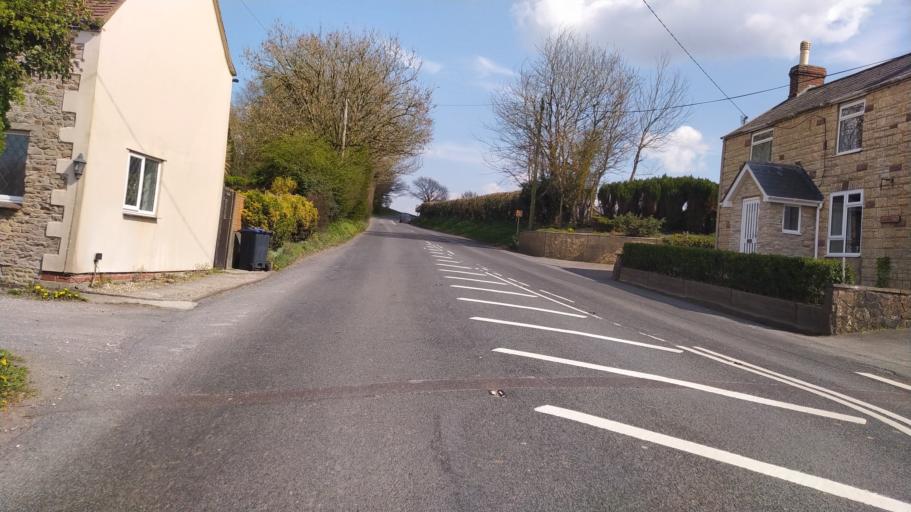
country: GB
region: England
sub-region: Wiltshire
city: Corsley
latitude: 51.2110
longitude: -2.2696
